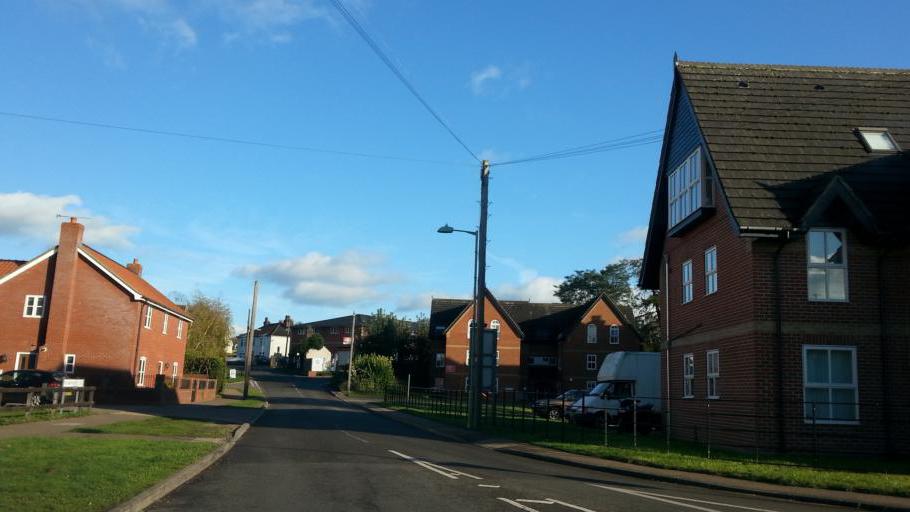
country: GB
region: England
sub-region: Suffolk
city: Thurston
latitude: 52.2504
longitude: 0.8078
